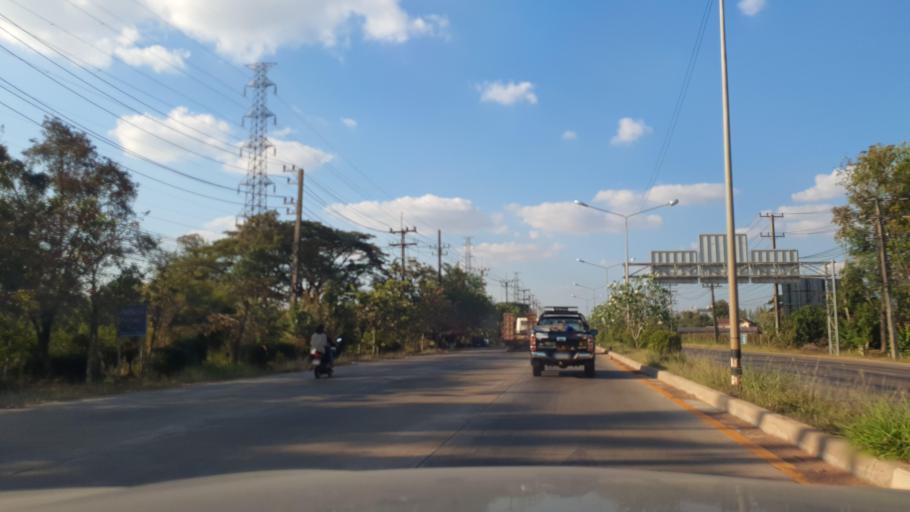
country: TH
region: Sakon Nakhon
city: Sakon Nakhon
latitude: 17.1424
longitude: 104.1105
